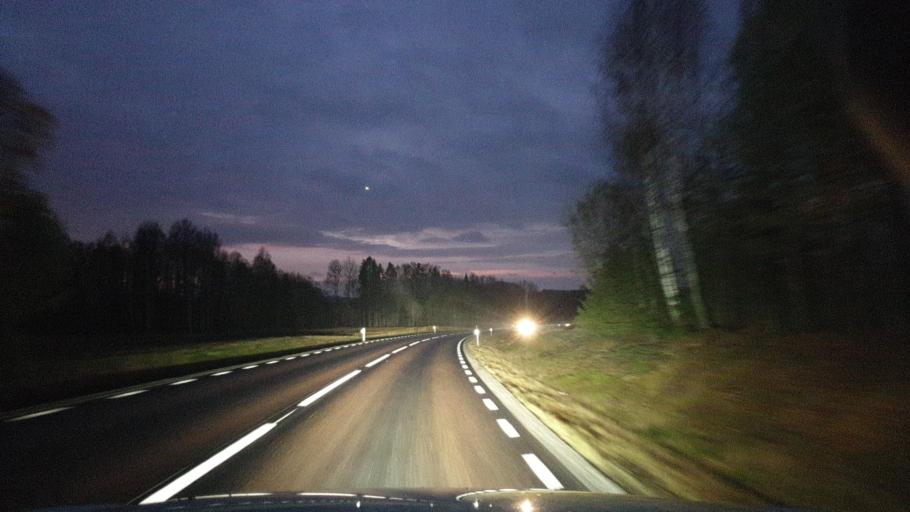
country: SE
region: Vaermland
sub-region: Eda Kommun
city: Charlottenberg
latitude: 59.8375
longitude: 12.3185
